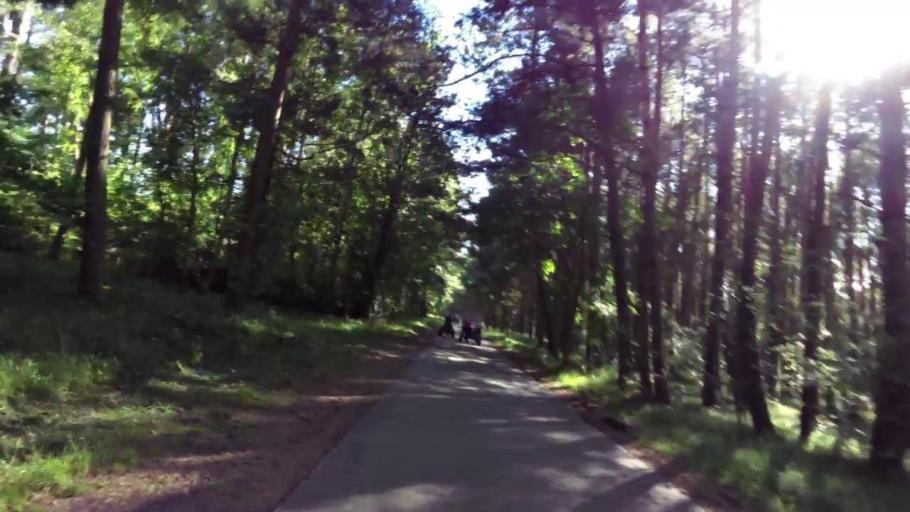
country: PL
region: West Pomeranian Voivodeship
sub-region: Powiat slawienski
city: Darlowo
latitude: 54.3729
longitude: 16.3032
